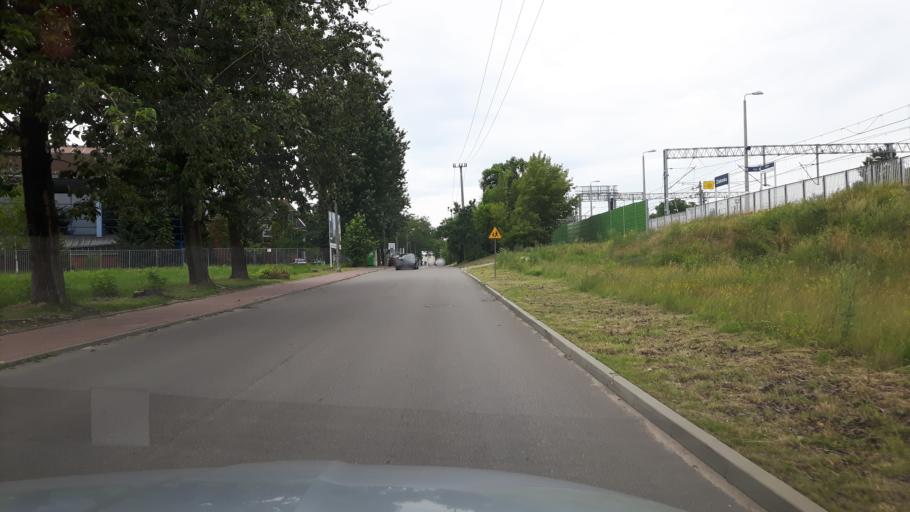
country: PL
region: Masovian Voivodeship
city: Zielonka
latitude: 52.3113
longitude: 21.1575
